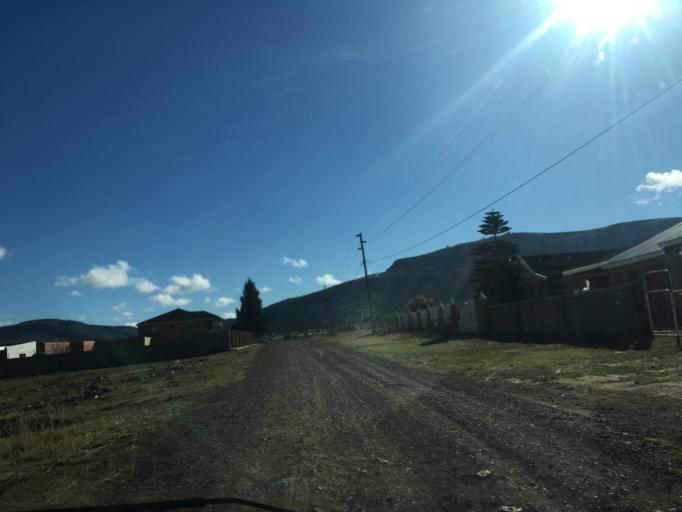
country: ZA
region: Eastern Cape
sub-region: Chris Hani District Municipality
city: Cala
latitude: -31.5388
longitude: 27.6940
